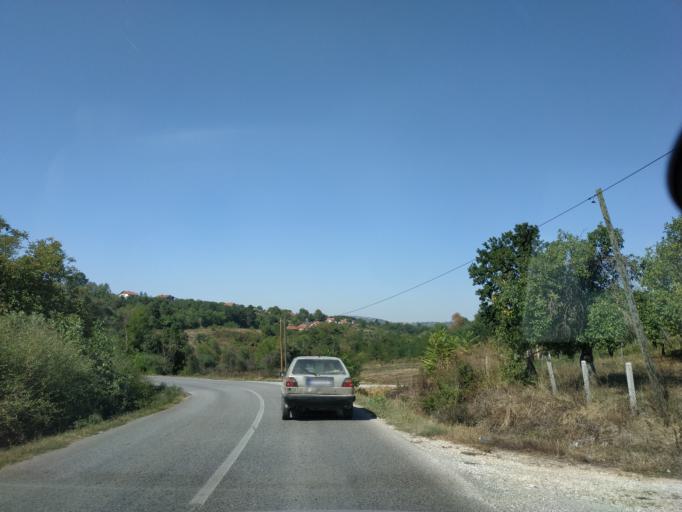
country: RS
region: Central Serbia
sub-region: Sumadijski Okrug
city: Topola
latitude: 44.2762
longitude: 20.6243
